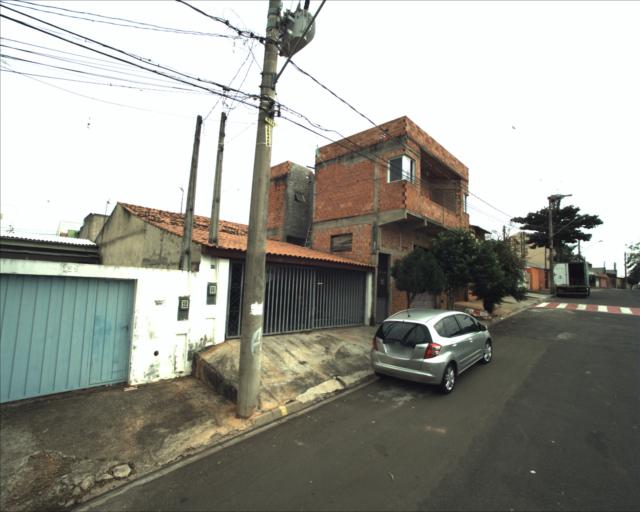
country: BR
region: Sao Paulo
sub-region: Sorocaba
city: Sorocaba
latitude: -23.4943
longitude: -47.5297
